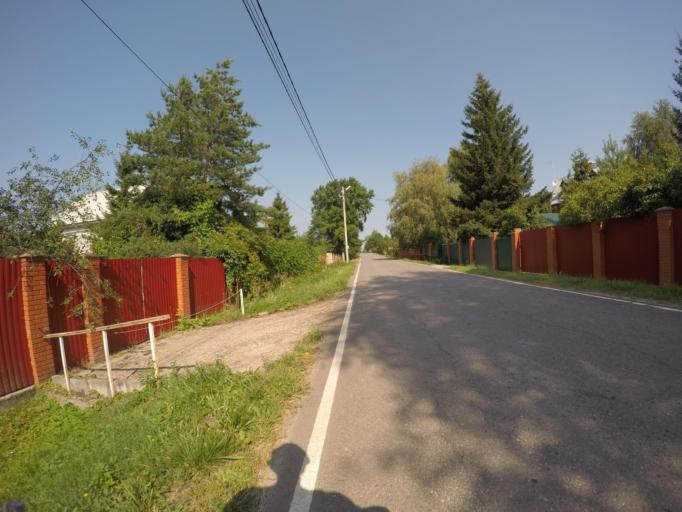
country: RU
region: Moskovskaya
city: Rechitsy
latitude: 55.6187
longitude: 38.5295
